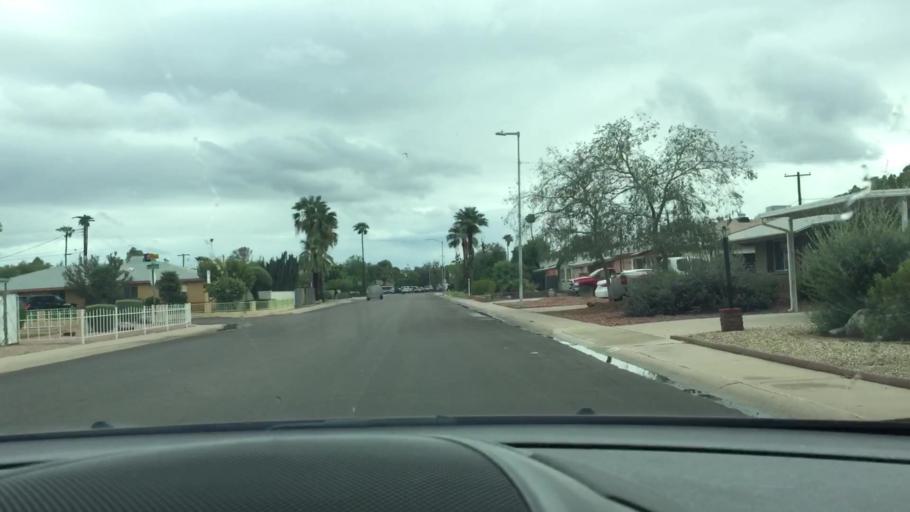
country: US
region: Arizona
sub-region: Maricopa County
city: Tempe
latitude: 33.4614
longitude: -111.9217
